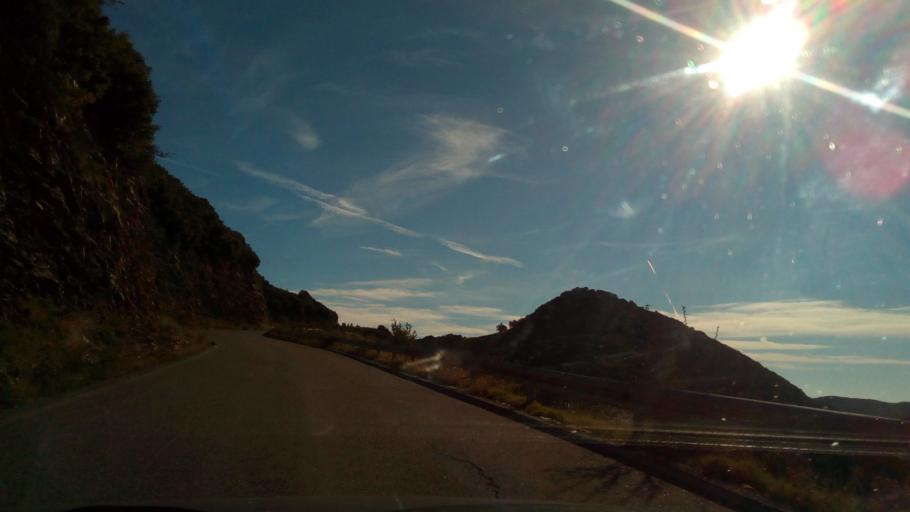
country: GR
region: West Greece
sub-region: Nomos Aitolias kai Akarnanias
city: Nafpaktos
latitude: 38.4838
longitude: 21.8649
